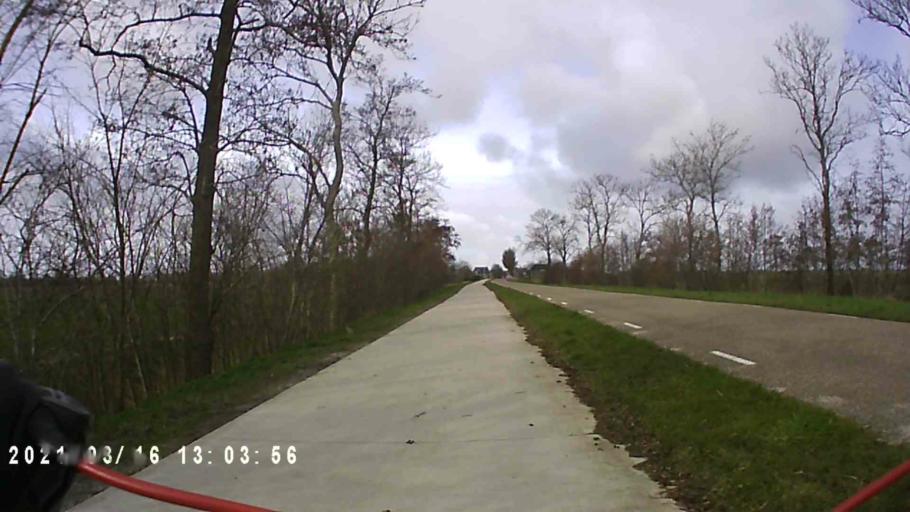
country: NL
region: Friesland
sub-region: Menameradiel
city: Berltsum
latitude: 53.2501
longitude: 5.6341
